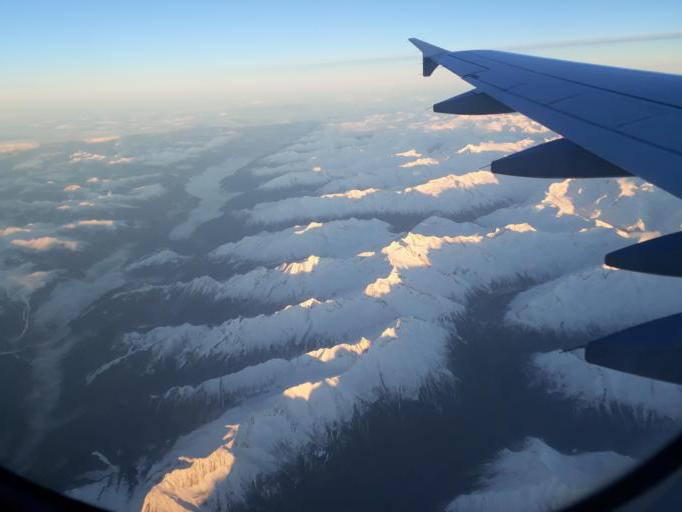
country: AT
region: Tyrol
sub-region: Politischer Bezirk Schwaz
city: Mayrhofen
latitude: 47.1373
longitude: 11.8812
